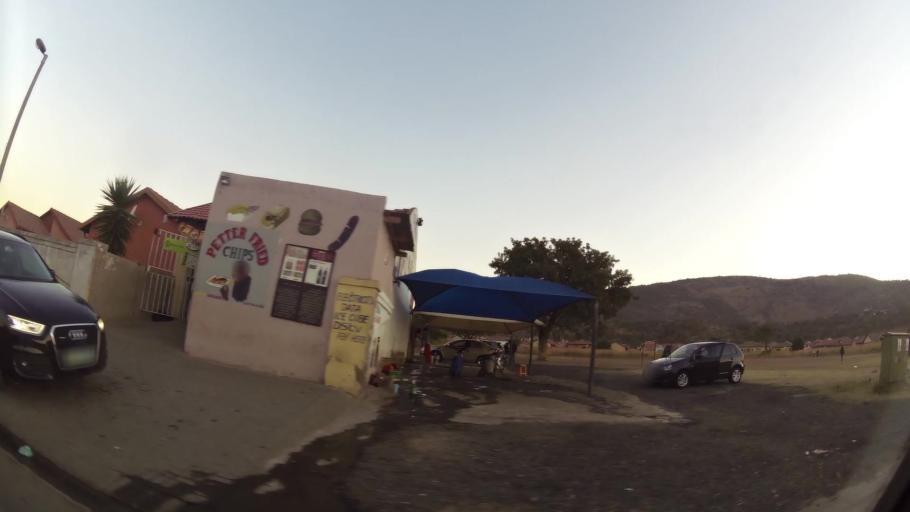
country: ZA
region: North-West
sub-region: Bojanala Platinum District Municipality
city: Rustenburg
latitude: -25.6433
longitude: 27.2021
